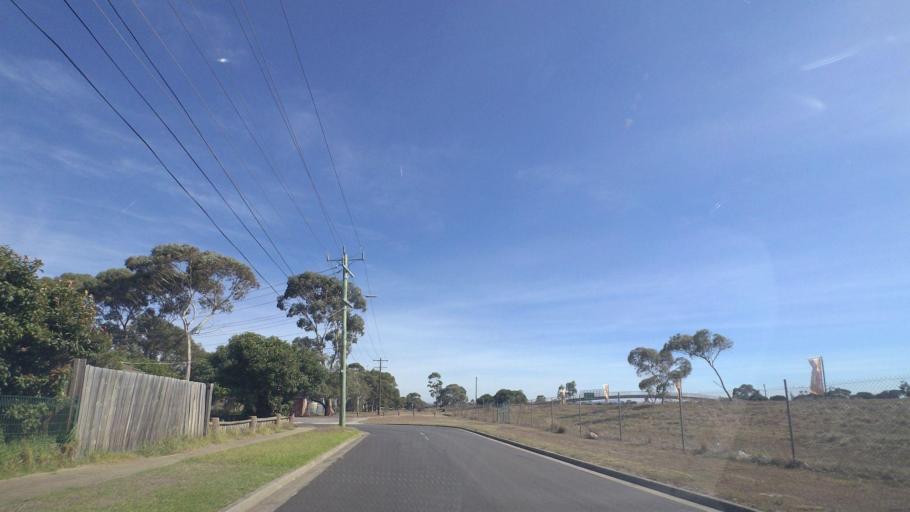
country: AU
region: Victoria
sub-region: Melton
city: Melton
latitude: -37.6918
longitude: 144.5743
